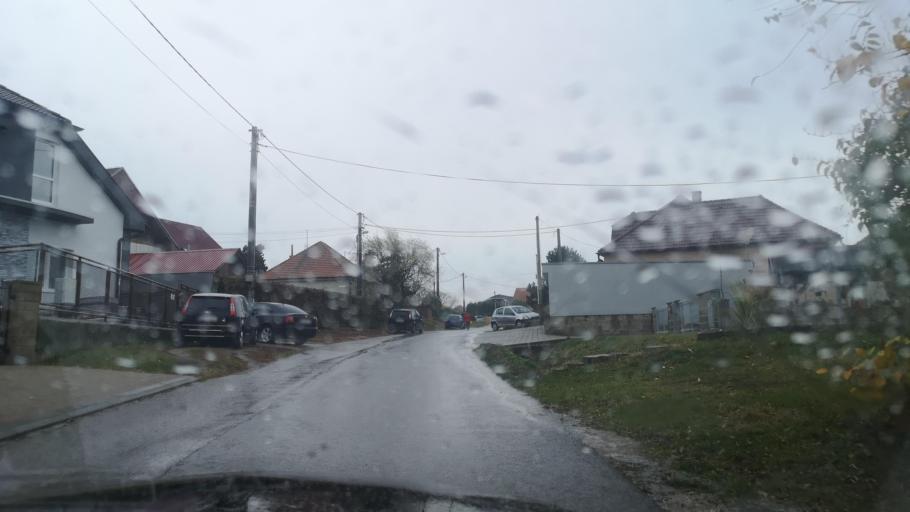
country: SK
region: Nitriansky
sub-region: Okres Nitra
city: Nitra
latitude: 48.2862
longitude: 18.1409
